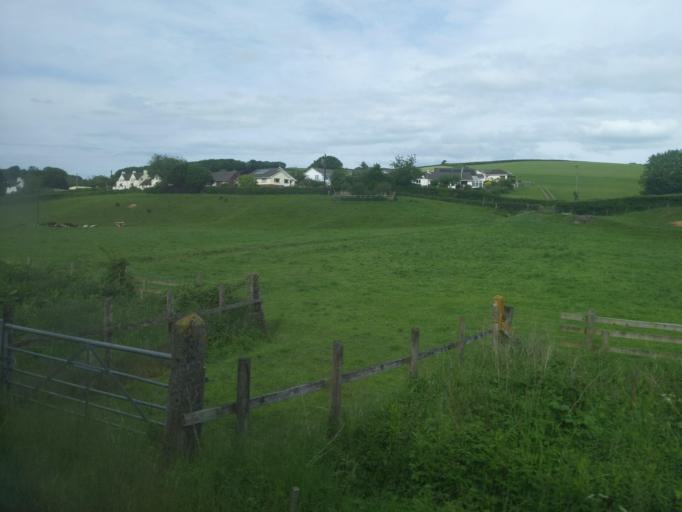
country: GB
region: England
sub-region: Devon
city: Barnstaple
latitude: 50.9908
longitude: -3.9841
